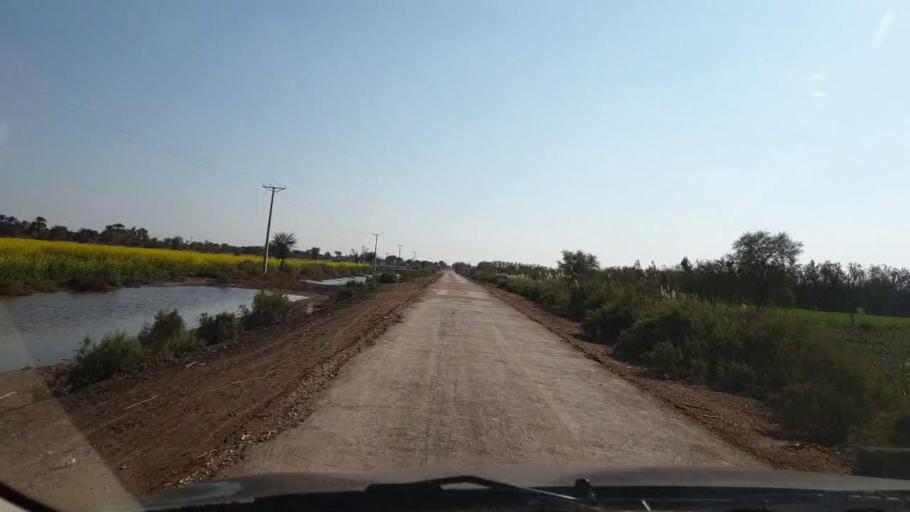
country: PK
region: Sindh
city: Sinjhoro
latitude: 25.9919
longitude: 68.8394
